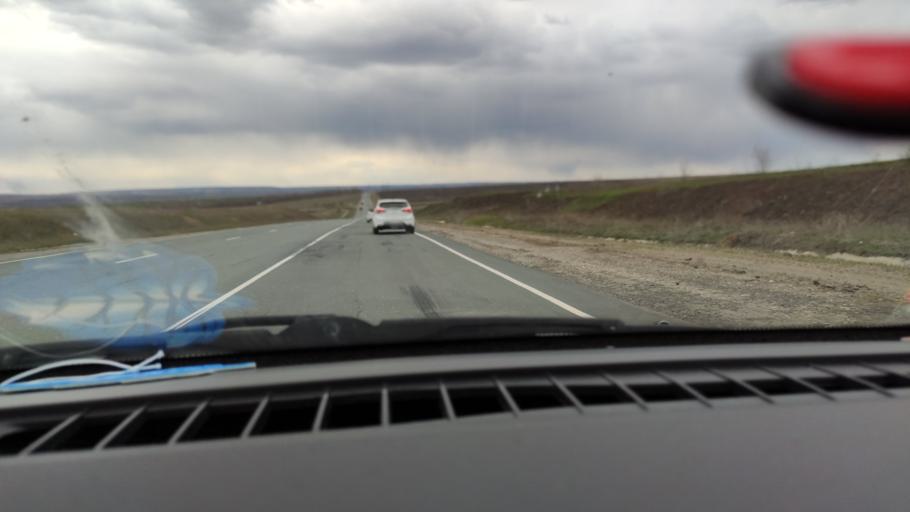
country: RU
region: Saratov
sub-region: Saratovskiy Rayon
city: Saratov
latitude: 51.7566
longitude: 46.0665
